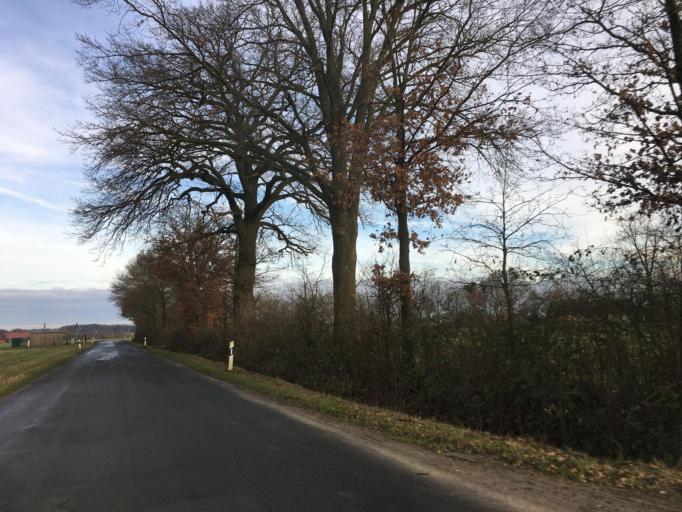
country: DE
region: North Rhine-Westphalia
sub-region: Regierungsbezirk Munster
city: Dulmen
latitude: 51.8293
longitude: 7.3321
